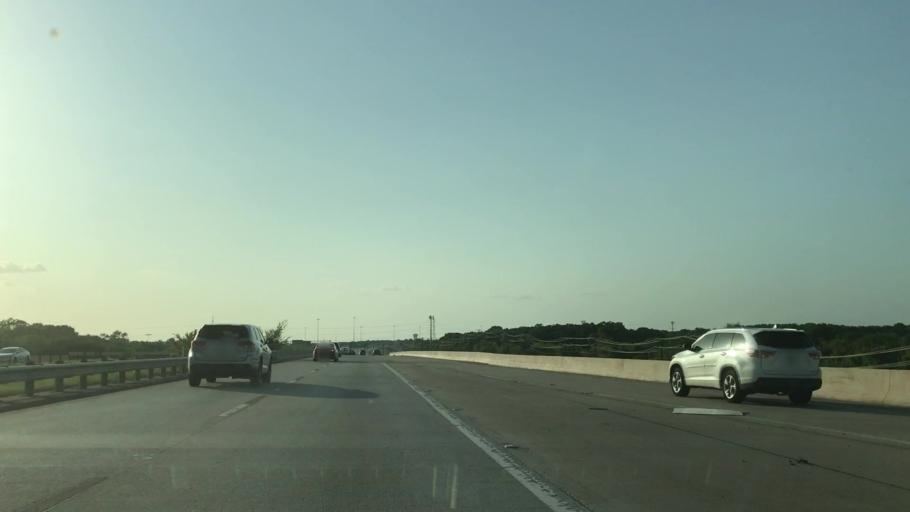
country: US
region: Texas
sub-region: Tarrant County
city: Grapevine
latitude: 32.8950
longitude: -97.0856
